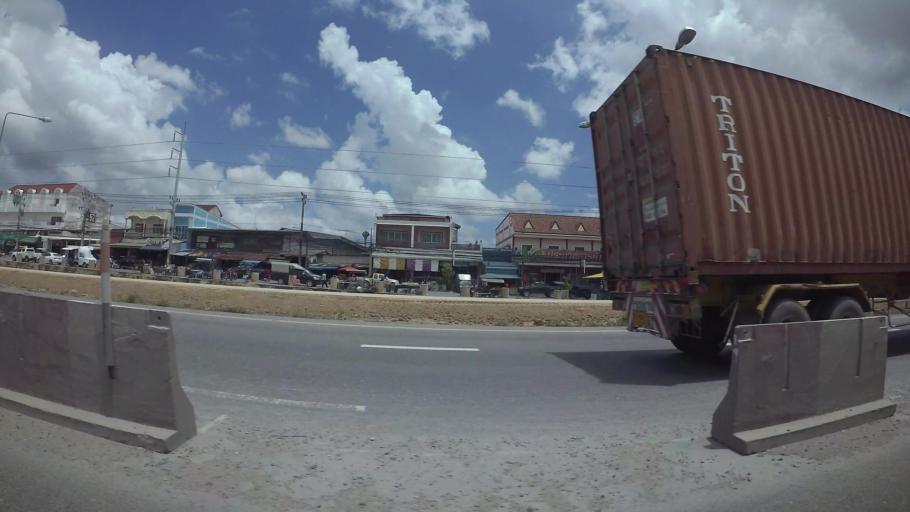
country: TH
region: Rayong
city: Nikhom Phattana
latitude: 12.8568
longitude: 101.0919
